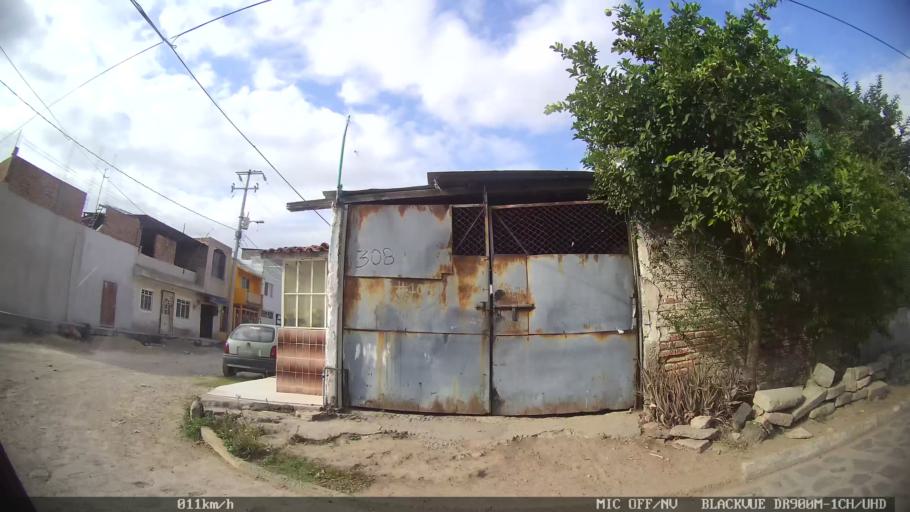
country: MX
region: Jalisco
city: Tonala
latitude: 20.6742
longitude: -103.2389
